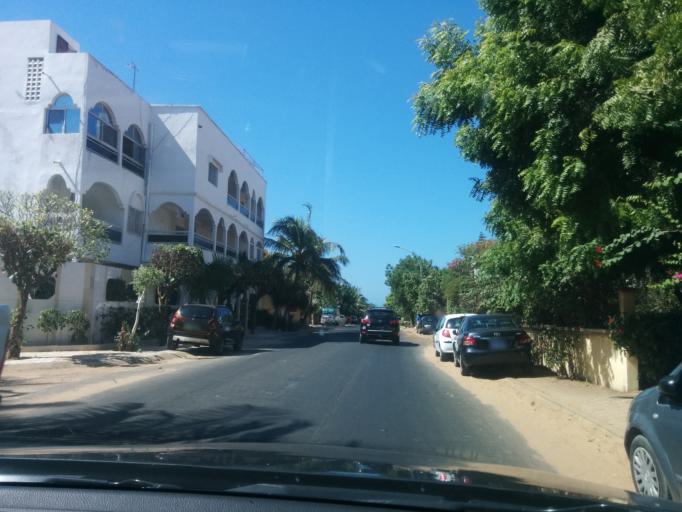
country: SN
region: Dakar
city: Mermoz Boabab
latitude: 14.7094
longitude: -17.4838
